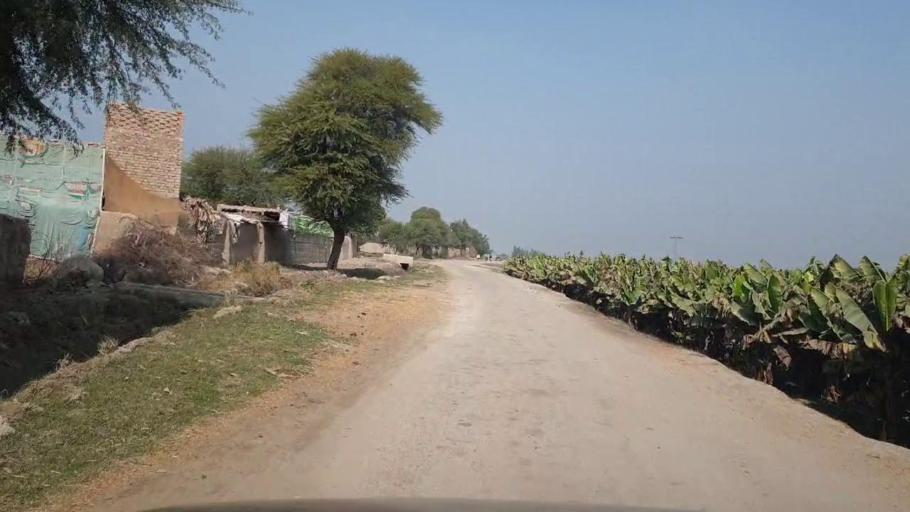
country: PK
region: Sindh
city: Bhit Shah
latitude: 25.7880
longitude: 68.4932
